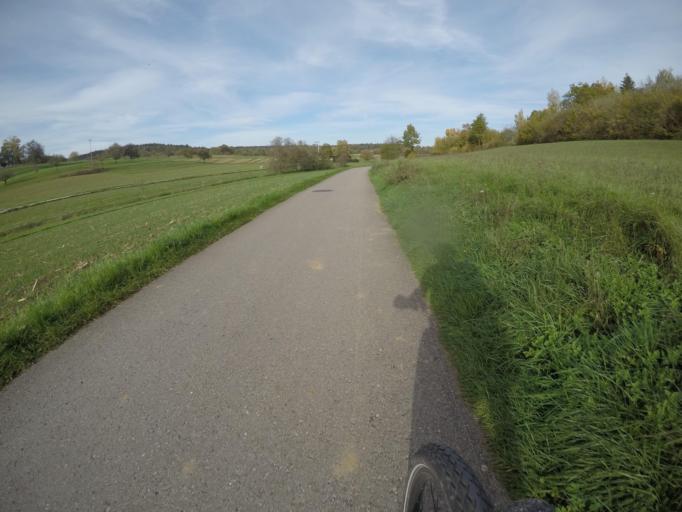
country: DE
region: Baden-Wuerttemberg
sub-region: Regierungsbezirk Stuttgart
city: Weil der Stadt
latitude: 48.7748
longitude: 8.8915
